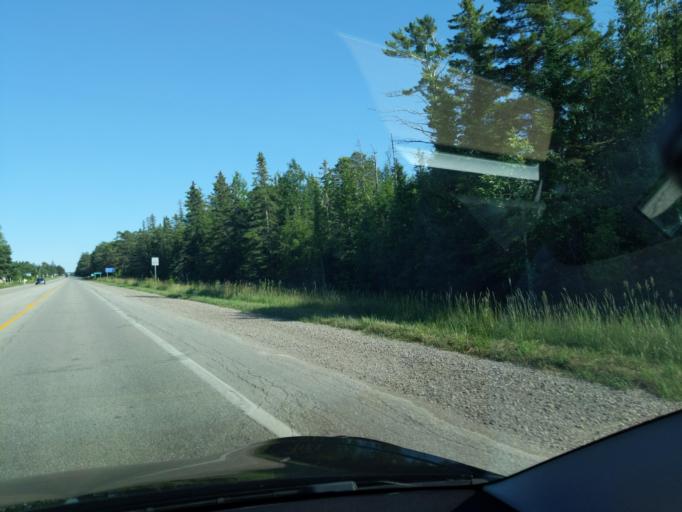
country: US
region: Michigan
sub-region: Mackinac County
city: Saint Ignace
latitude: 45.7630
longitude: -84.7153
